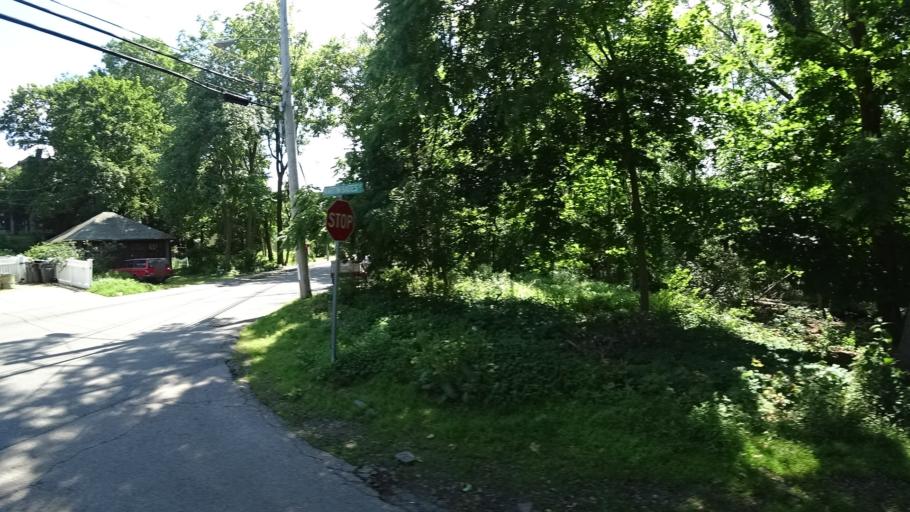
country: US
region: Massachusetts
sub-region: Norfolk County
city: Dedham
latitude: 42.2452
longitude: -71.1801
